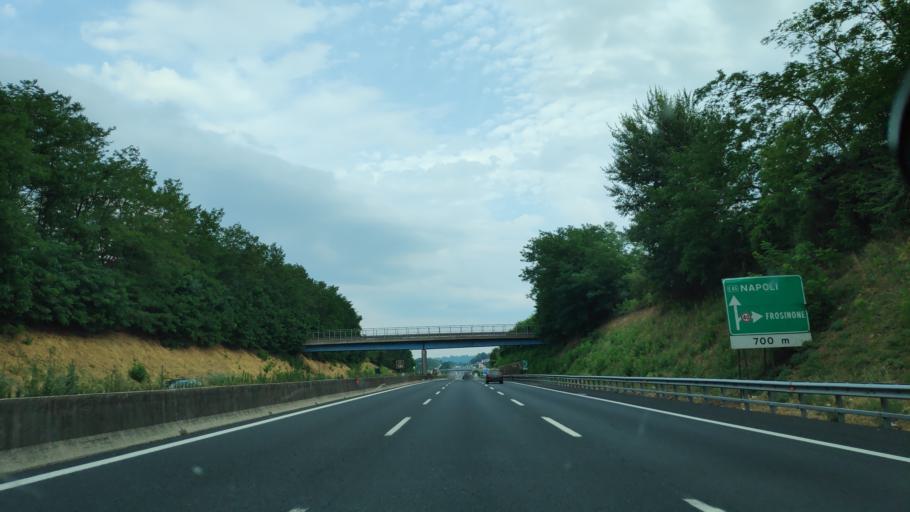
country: IT
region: Latium
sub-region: Provincia di Frosinone
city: Frosinone
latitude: 41.6240
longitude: 13.2996
